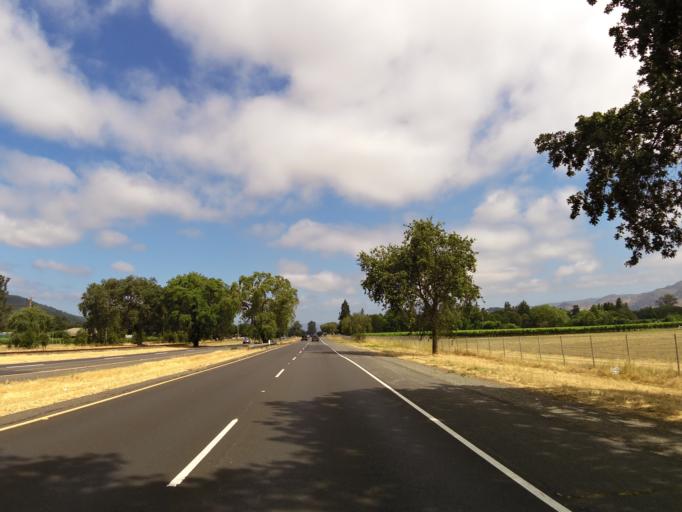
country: US
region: California
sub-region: Napa County
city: Yountville
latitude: 38.3621
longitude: -122.3361
